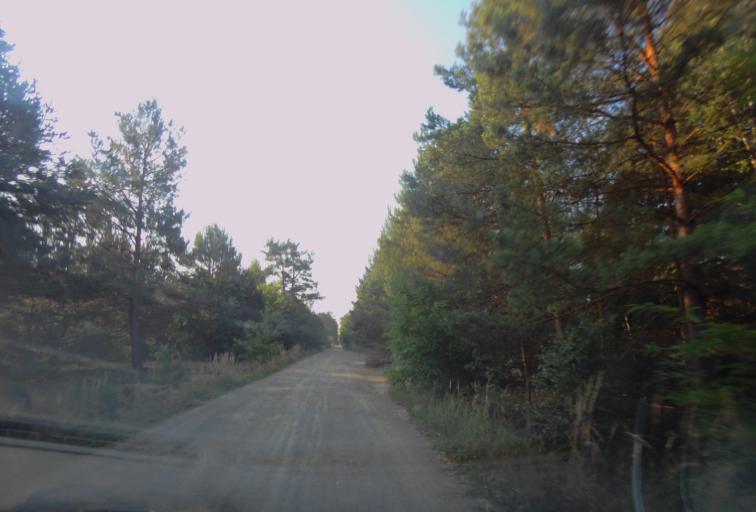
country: PL
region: Lublin Voivodeship
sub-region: Powiat janowski
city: Dzwola
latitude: 50.5987
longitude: 22.5165
